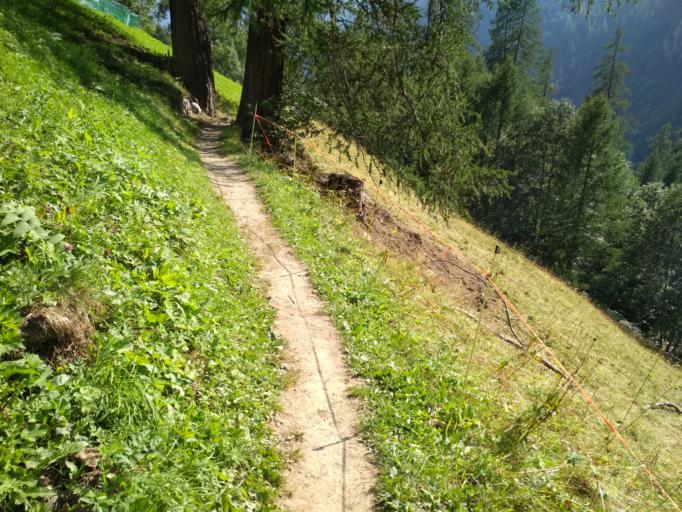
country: IT
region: Aosta Valley
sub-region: Valle d'Aosta
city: Gressoney-La-Trinite
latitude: 45.8044
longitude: 7.8267
